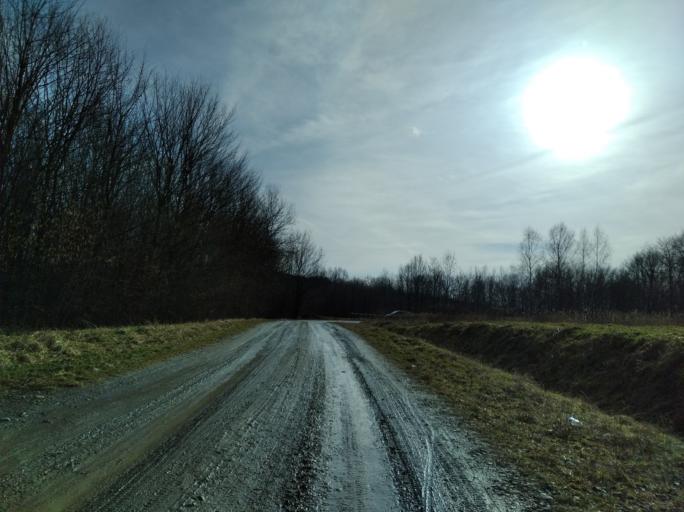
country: PL
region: Subcarpathian Voivodeship
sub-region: Powiat brzozowski
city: Gorki
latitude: 49.6405
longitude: 22.0615
